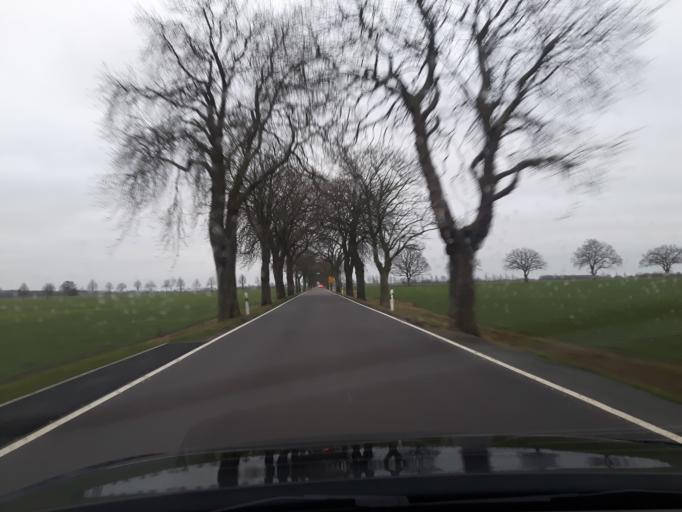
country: DE
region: Mecklenburg-Vorpommern
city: Bad Sulze
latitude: 54.0551
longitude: 12.6727
